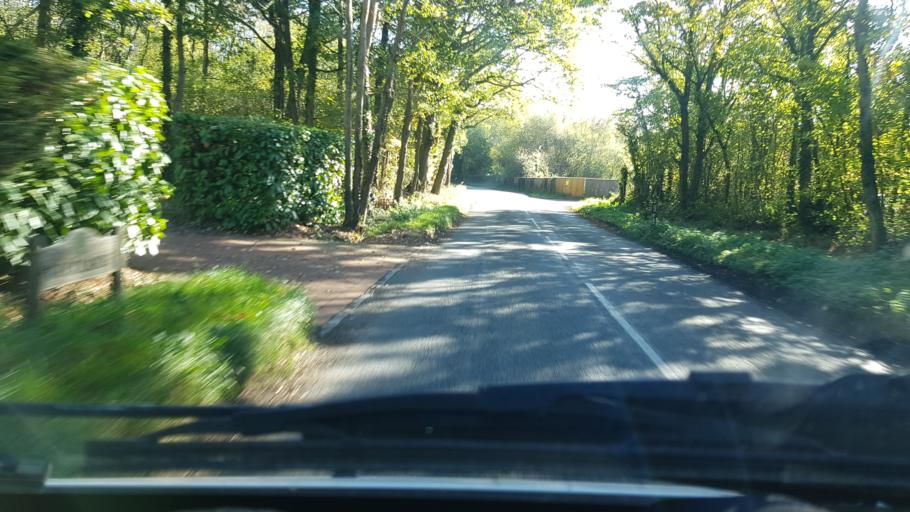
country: GB
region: England
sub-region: Surrey
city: Ockley
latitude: 51.1328
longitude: -0.4173
